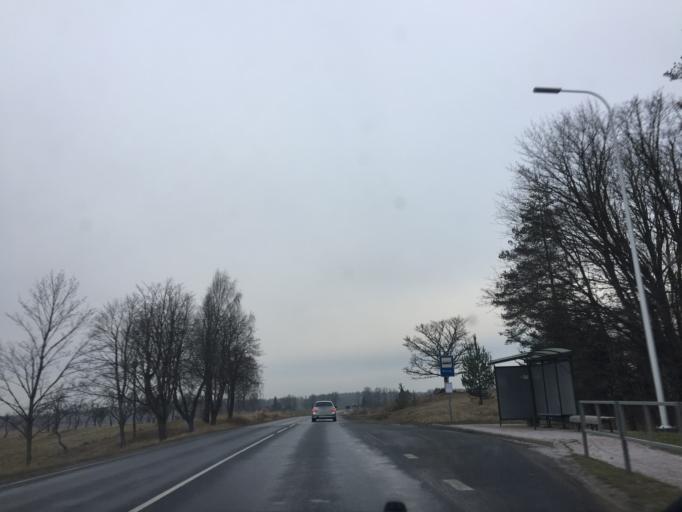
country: LV
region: Raunas
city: Rauna
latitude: 57.2807
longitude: 25.4949
